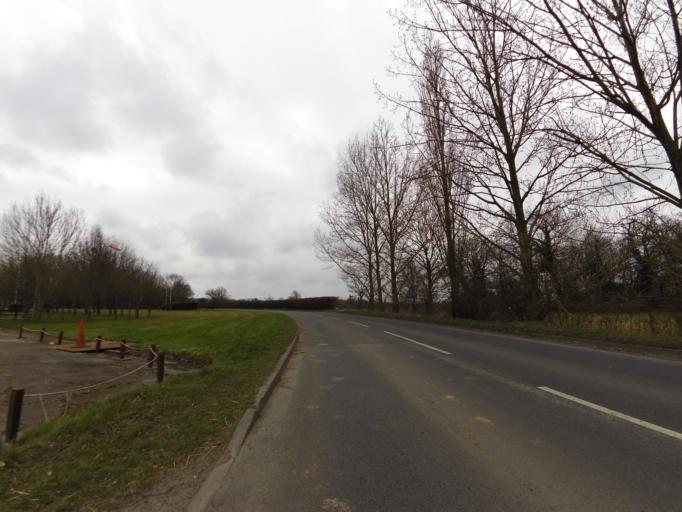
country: GB
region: England
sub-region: Suffolk
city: Halesworth
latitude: 52.3549
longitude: 1.5224
